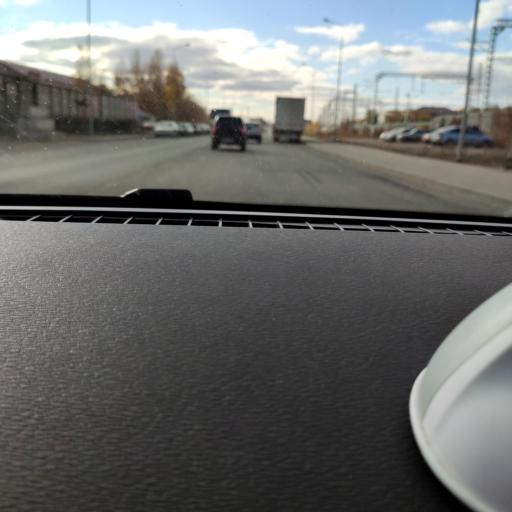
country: RU
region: Samara
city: Samara
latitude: 53.1798
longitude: 50.2079
